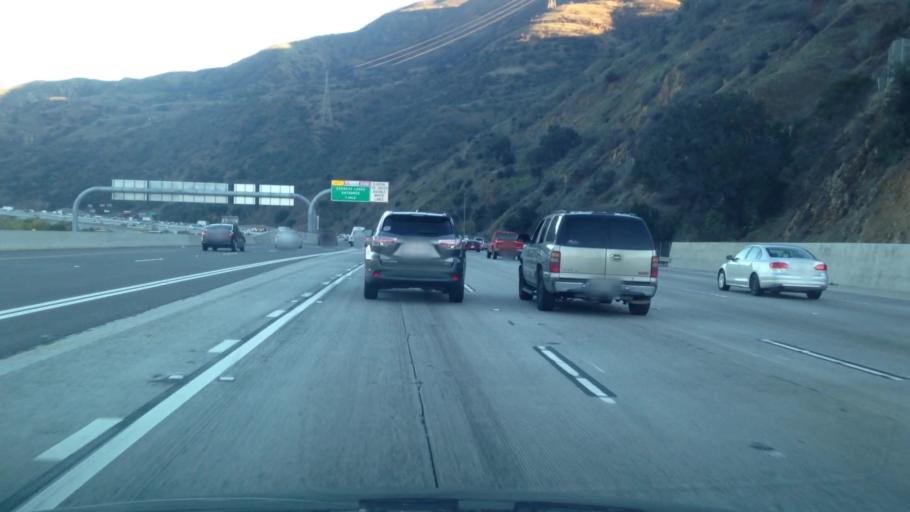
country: US
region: California
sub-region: San Bernardino County
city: Los Serranos
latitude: 33.8705
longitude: -117.6838
